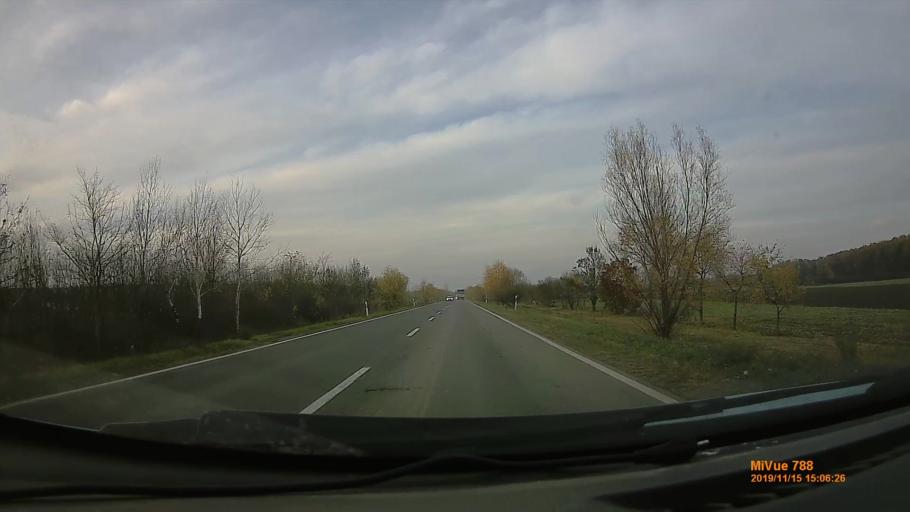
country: HU
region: Bekes
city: Gyula
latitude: 46.6426
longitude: 21.2450
